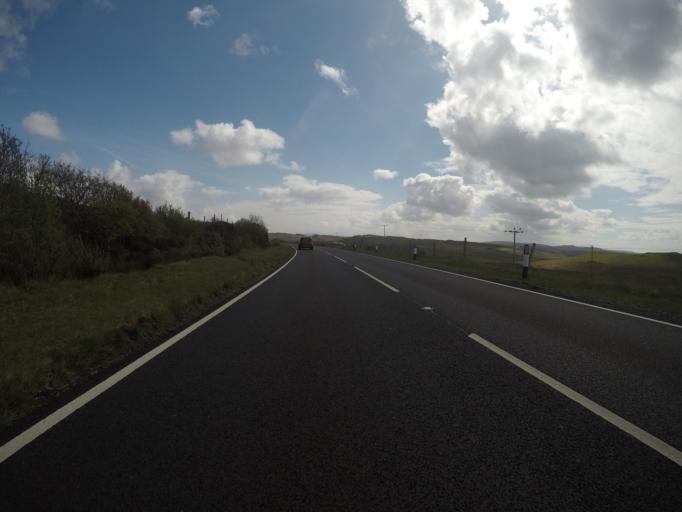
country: GB
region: Scotland
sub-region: Highland
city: Portree
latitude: 57.5356
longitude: -6.3609
